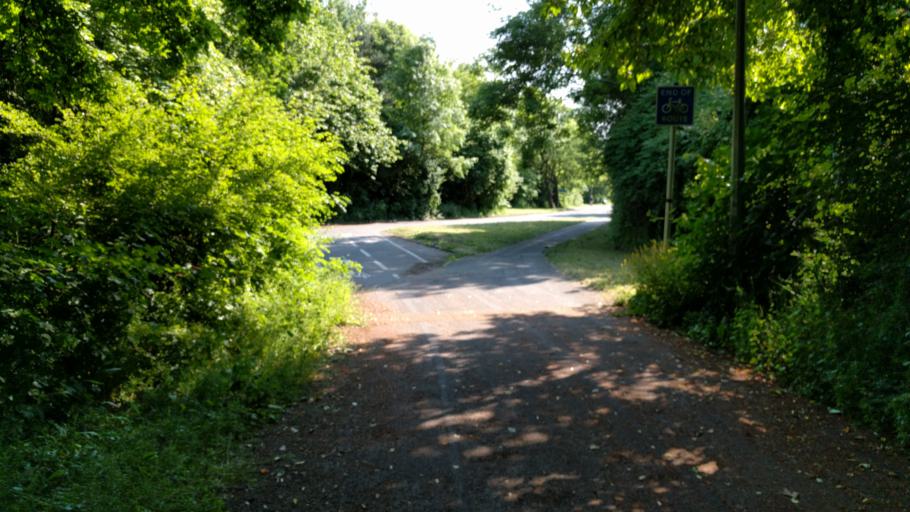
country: GB
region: England
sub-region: Warrington
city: Croft
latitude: 53.4213
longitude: -2.5310
